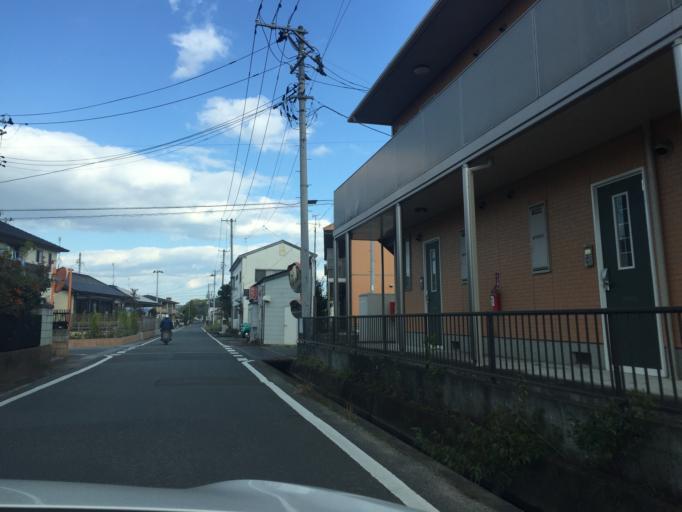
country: JP
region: Fukushima
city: Iwaki
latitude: 37.0611
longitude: 140.8680
